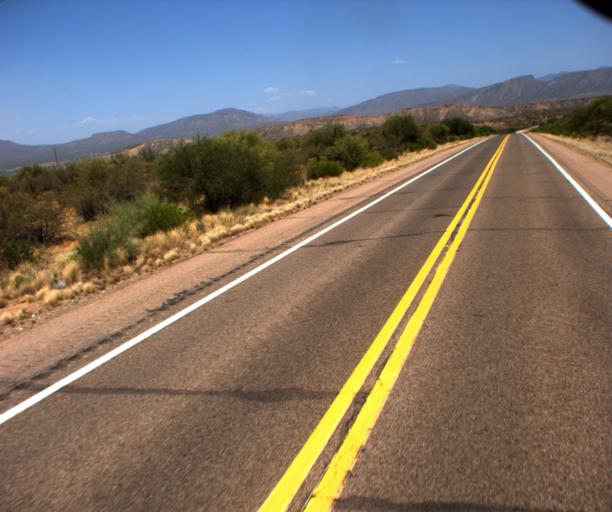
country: US
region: Arizona
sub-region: Gila County
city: Miami
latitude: 33.6146
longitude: -111.0292
